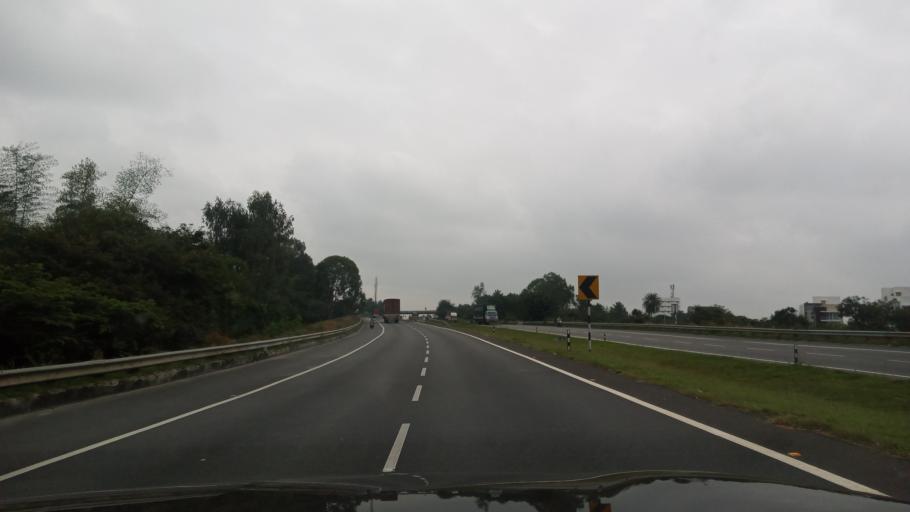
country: IN
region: Karnataka
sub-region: Bangalore Urban
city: Bangalore
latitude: 12.8539
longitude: 77.6046
